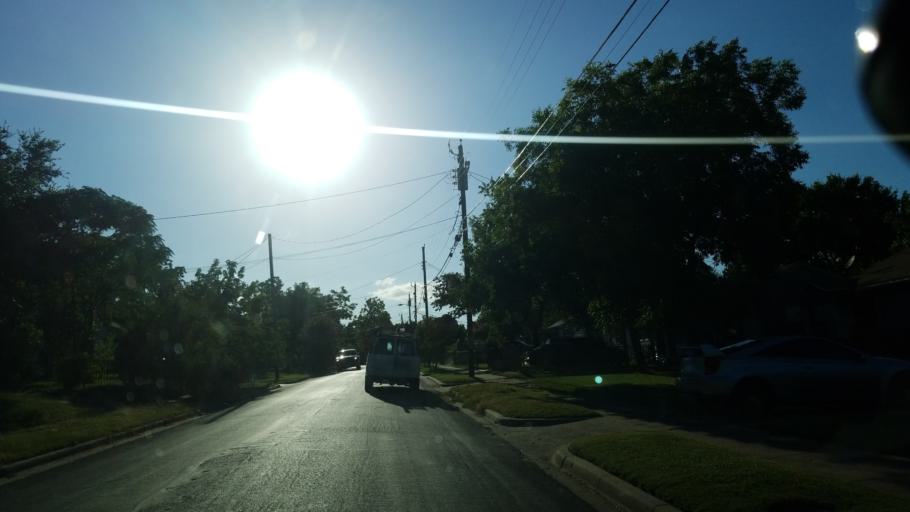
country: US
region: Texas
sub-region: Dallas County
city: Balch Springs
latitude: 32.7770
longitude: -96.7063
